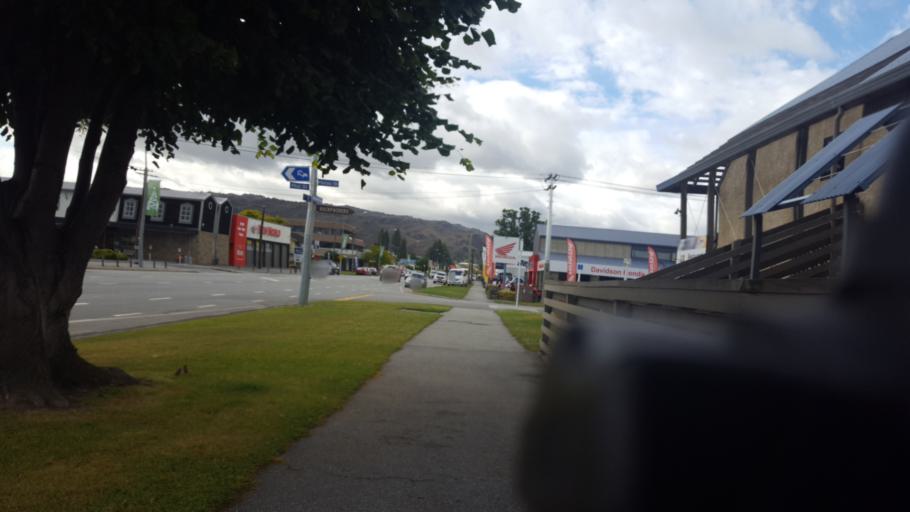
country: NZ
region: Otago
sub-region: Queenstown-Lakes District
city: Wanaka
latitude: -45.2497
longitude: 169.3860
